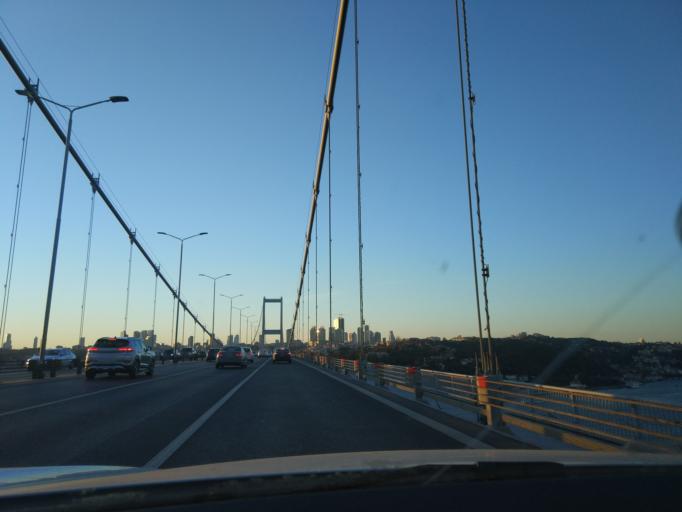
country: TR
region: Istanbul
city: UEskuedar
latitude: 41.0435
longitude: 29.0366
